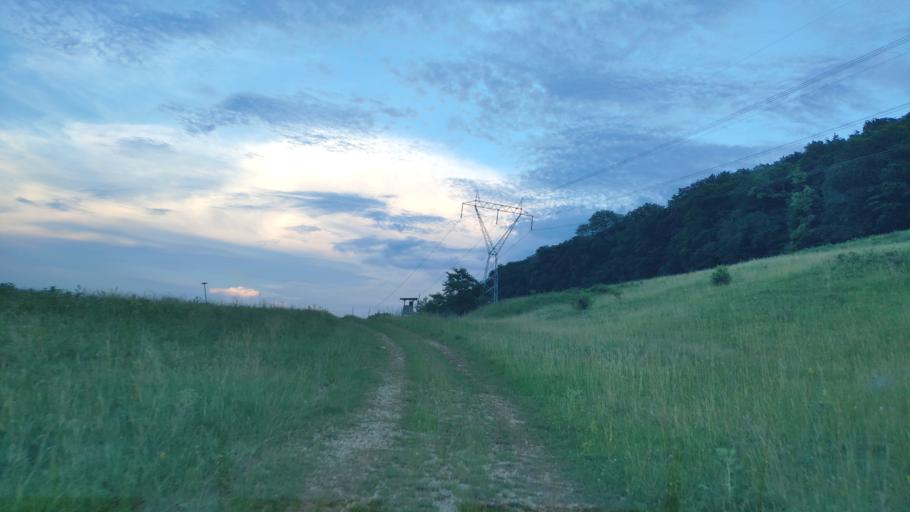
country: HU
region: Borsod-Abauj-Zemplen
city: Szendro
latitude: 48.5850
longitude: 20.7431
